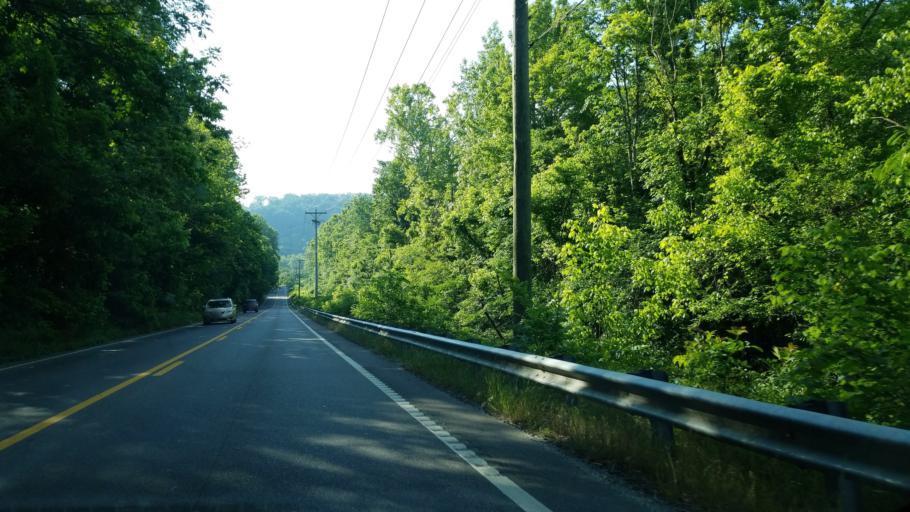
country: US
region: Tennessee
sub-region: Hamilton County
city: Collegedale
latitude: 35.0787
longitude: -85.0482
